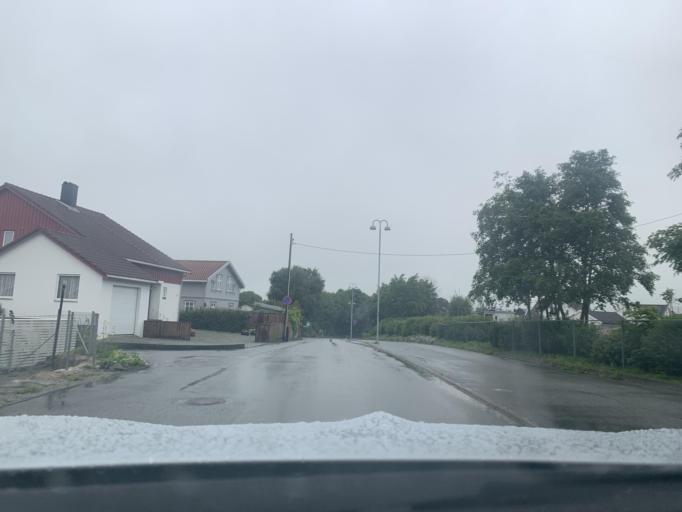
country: NO
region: Rogaland
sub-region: Time
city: Bryne
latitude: 58.7323
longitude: 5.6428
